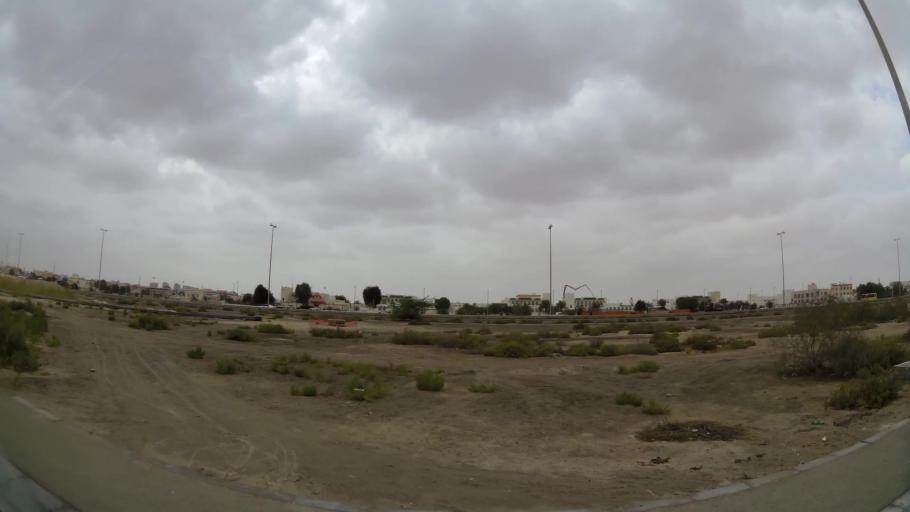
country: AE
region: Abu Dhabi
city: Abu Dhabi
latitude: 24.3281
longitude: 54.6388
